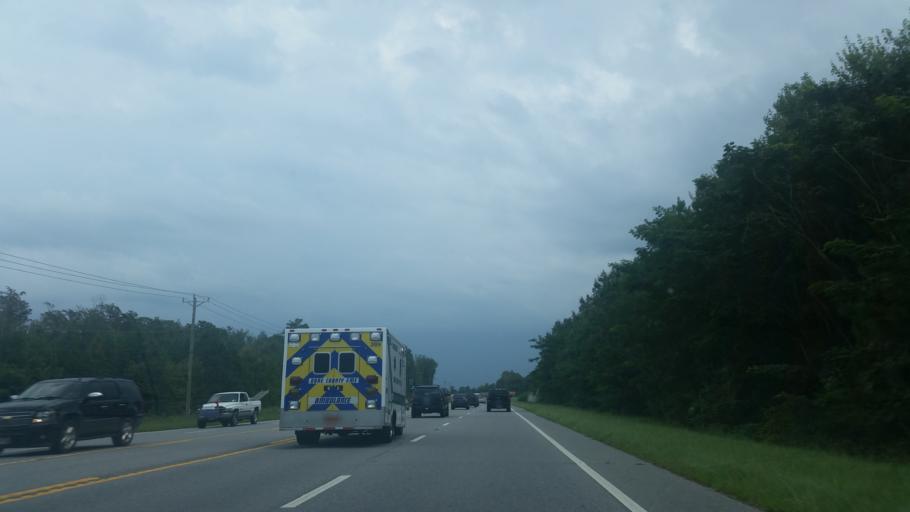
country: US
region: North Carolina
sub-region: Currituck County
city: Moyock
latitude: 36.4850
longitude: -76.1339
